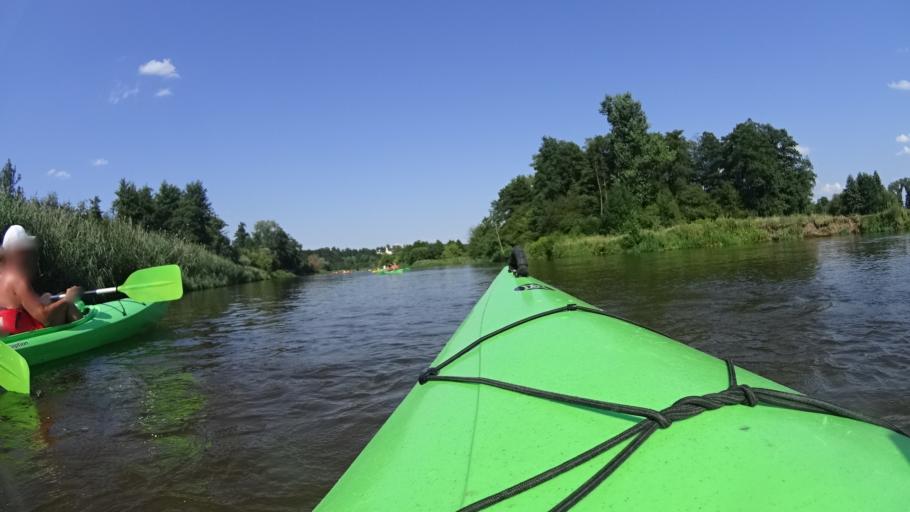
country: PL
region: Masovian Voivodeship
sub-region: Powiat bialobrzeski
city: Bialobrzegi
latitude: 51.6625
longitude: 20.9060
